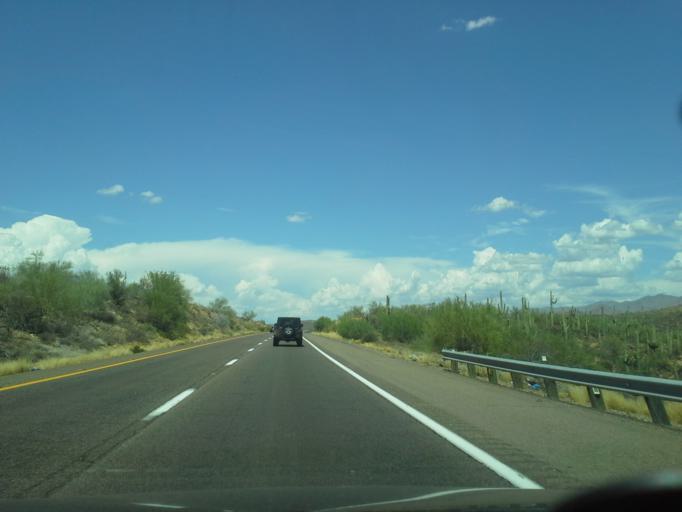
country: US
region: Arizona
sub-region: Maricopa County
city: New River
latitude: 33.9241
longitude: -112.1430
